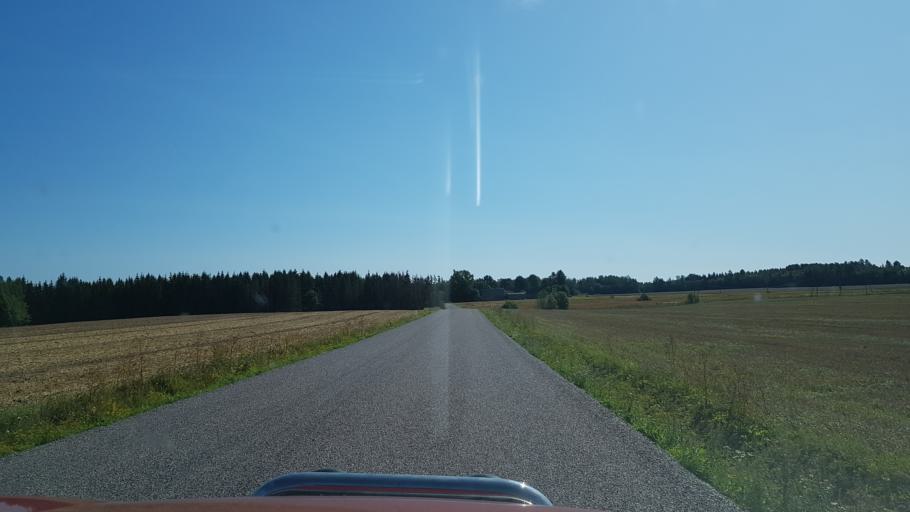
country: EE
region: Tartu
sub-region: Puhja vald
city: Puhja
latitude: 58.2586
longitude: 26.3132
